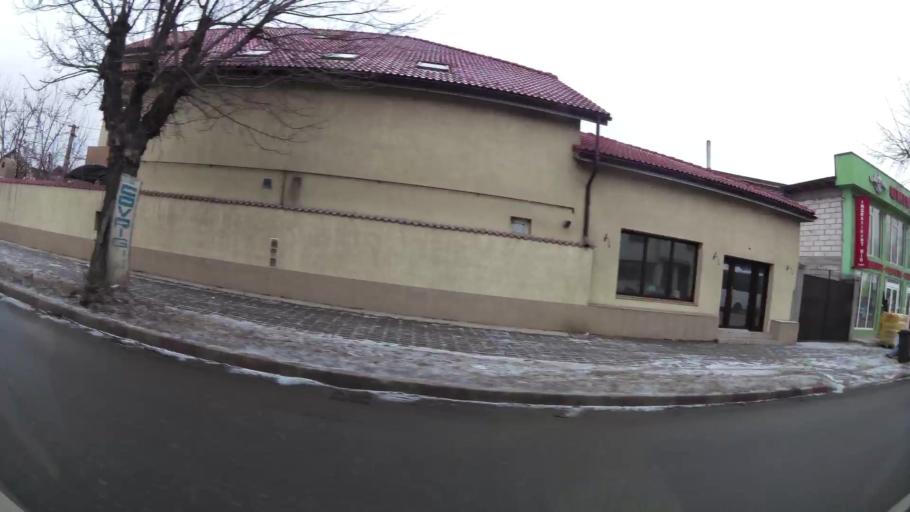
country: RO
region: Dambovita
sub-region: Comuna Ulmi
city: Ulmi
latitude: 44.9103
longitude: 25.4875
